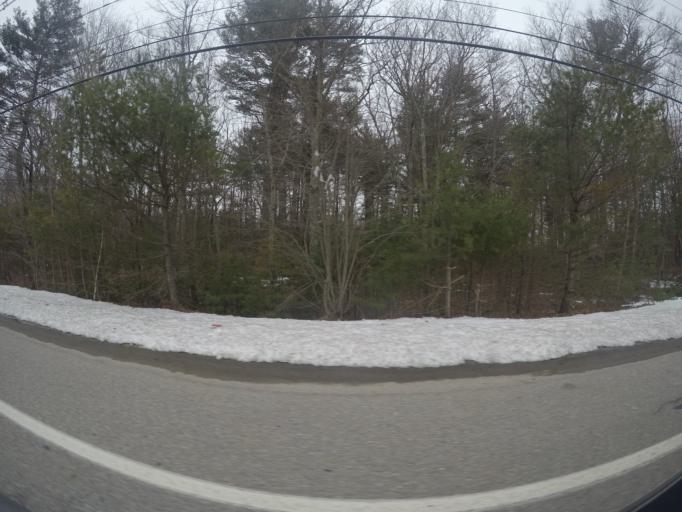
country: US
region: Massachusetts
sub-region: Bristol County
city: Easton
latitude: 42.0251
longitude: -71.1553
